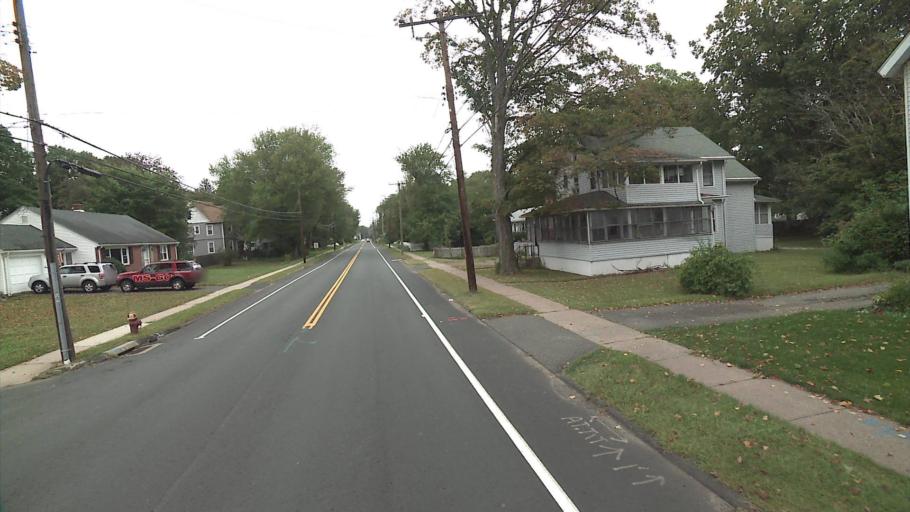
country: US
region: Connecticut
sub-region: Hartford County
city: Windsor
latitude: 41.8588
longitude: -72.6513
